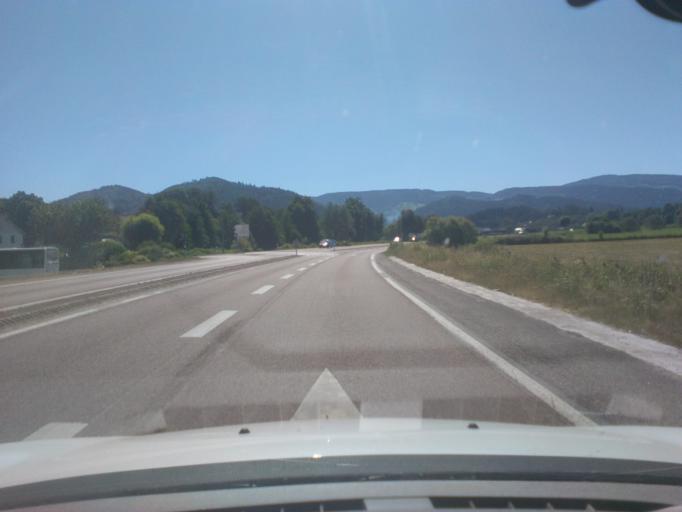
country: FR
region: Lorraine
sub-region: Departement des Vosges
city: Le Syndicat
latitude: 48.0246
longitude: 6.7006
